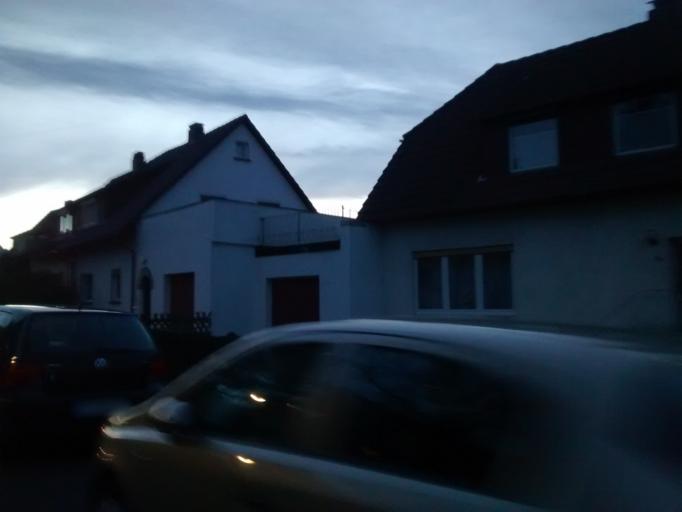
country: DE
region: Lower Saxony
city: Wolfenbuettel
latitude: 52.1694
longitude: 10.5221
